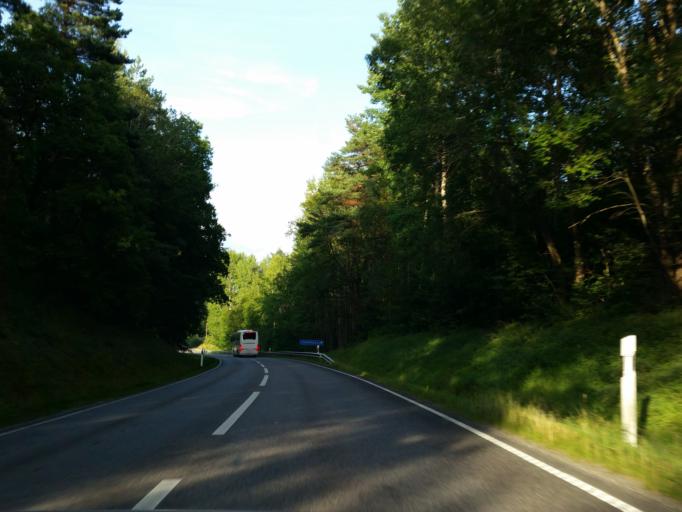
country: SE
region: Stockholm
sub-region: Sodertalje Kommun
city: Molnbo
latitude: 59.0400
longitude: 17.3926
